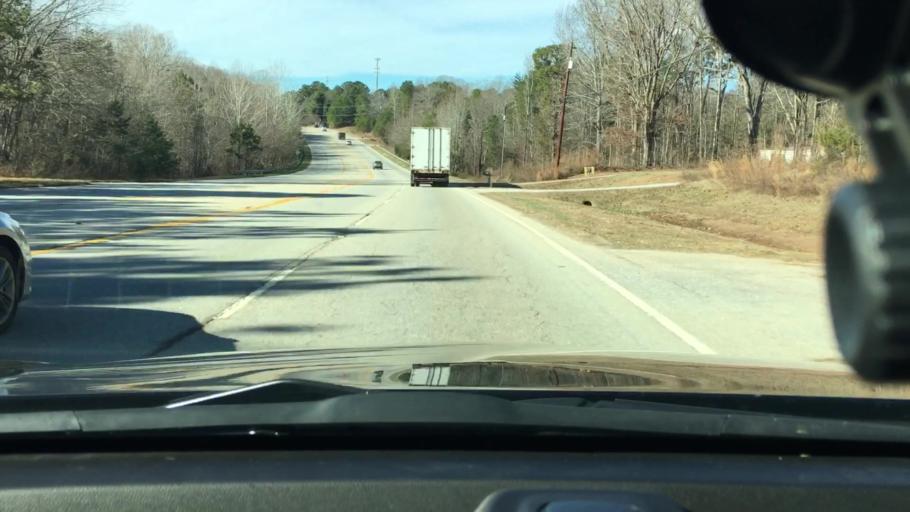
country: US
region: South Carolina
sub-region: Spartanburg County
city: Pacolet
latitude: 34.9234
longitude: -81.8260
